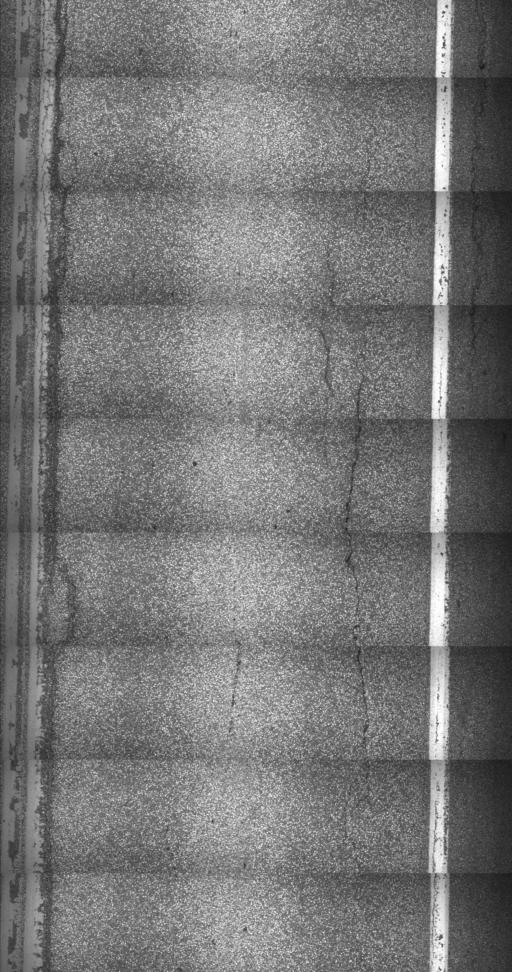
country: US
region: Vermont
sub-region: Washington County
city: Northfield
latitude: 44.1090
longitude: -72.6486
